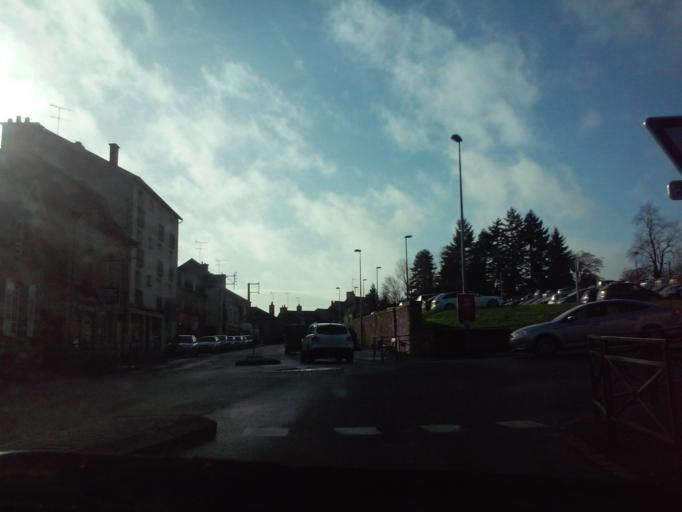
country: FR
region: Brittany
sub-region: Departement d'Ille-et-Vilaine
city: Fougeres
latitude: 48.3588
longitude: -1.1931
